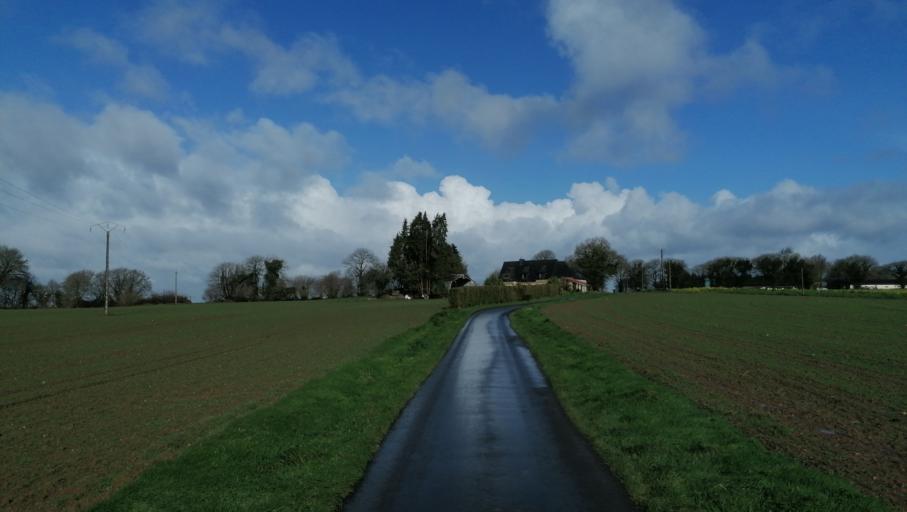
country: FR
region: Brittany
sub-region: Departement des Cotes-d'Armor
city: Lanrodec
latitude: 48.4850
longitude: -3.0204
